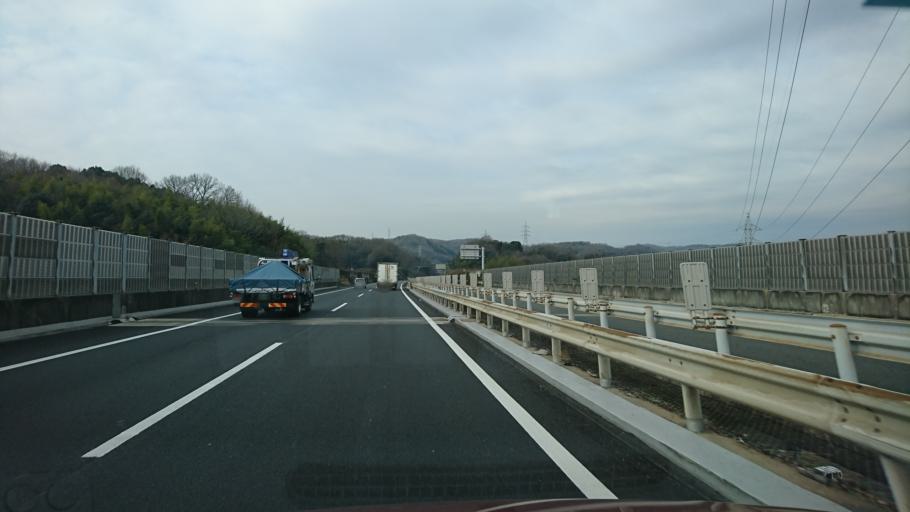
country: JP
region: Okayama
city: Kasaoka
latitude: 34.5350
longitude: 133.5073
